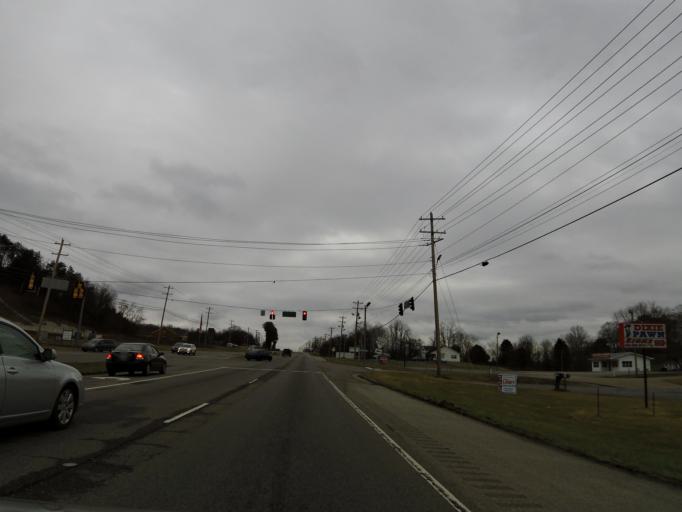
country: US
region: Tennessee
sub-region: Hamblen County
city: Morristown
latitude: 36.1850
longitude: -83.3745
